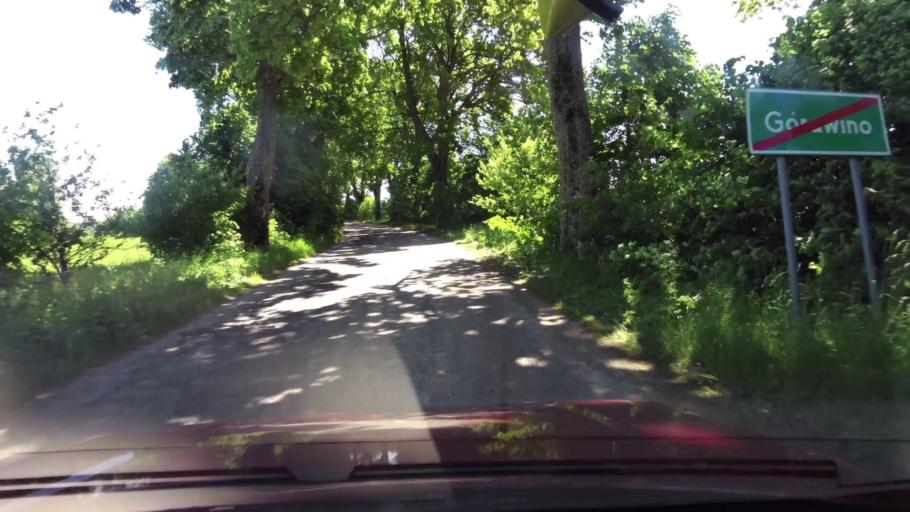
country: PL
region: West Pomeranian Voivodeship
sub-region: Powiat koszalinski
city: Bobolice
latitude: 54.0147
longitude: 16.6537
